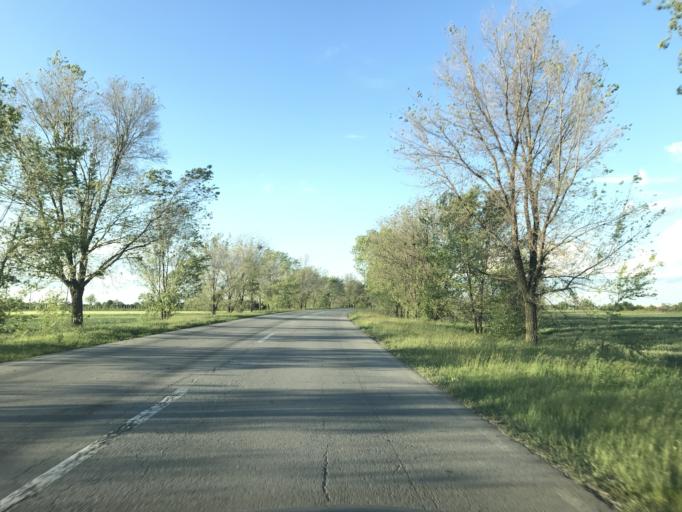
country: RS
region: Autonomna Pokrajina Vojvodina
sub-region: Srednjebanatski Okrug
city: Zrenjanin
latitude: 45.3917
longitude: 20.3536
